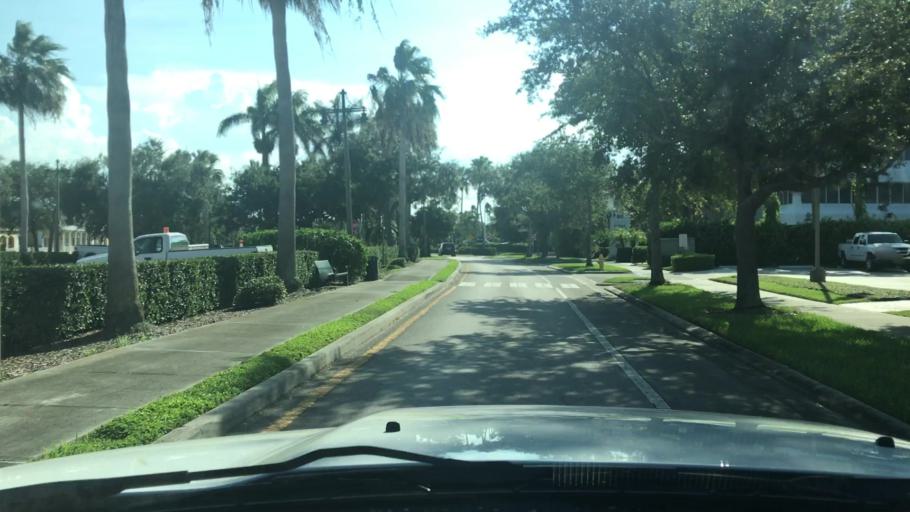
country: US
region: Florida
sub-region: Indian River County
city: Vero Beach
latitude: 27.6470
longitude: -80.3797
